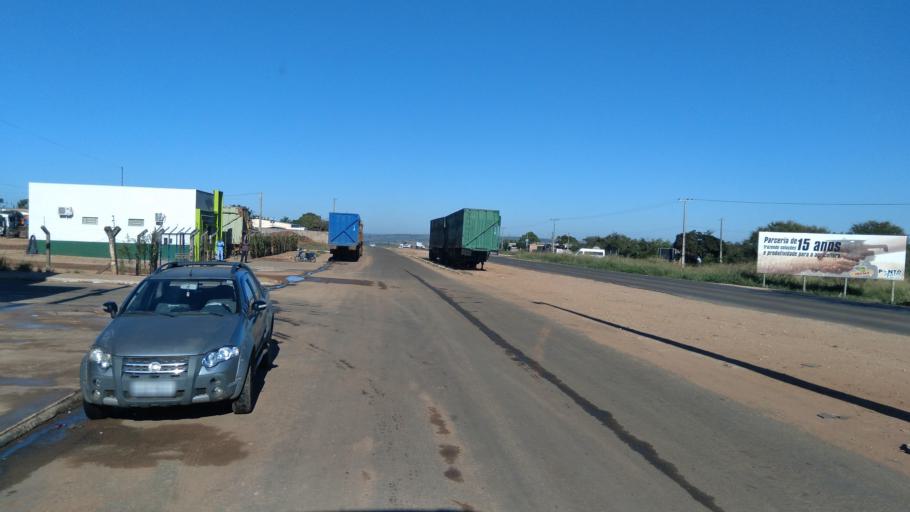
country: BR
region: Goias
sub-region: Mineiros
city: Mineiros
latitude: -17.5877
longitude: -52.5563
